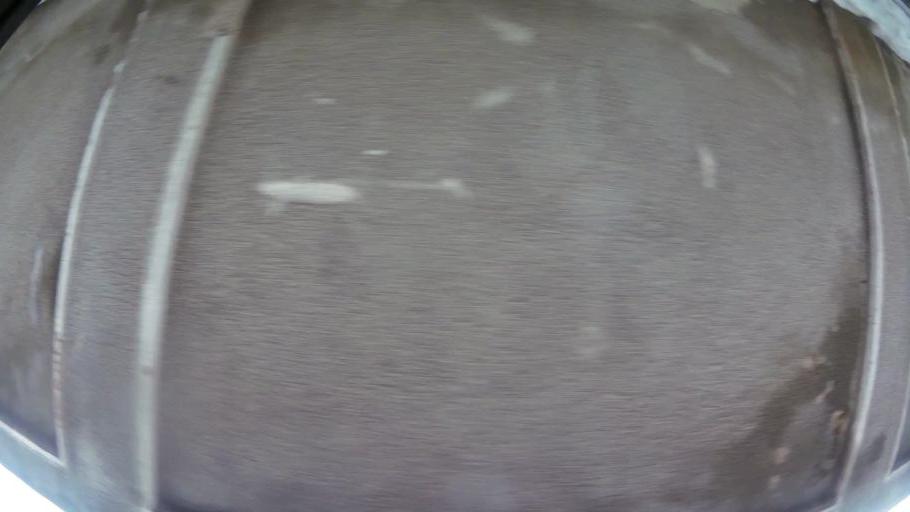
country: RO
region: Bucuresti
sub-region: Municipiul Bucuresti
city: Bucuresti
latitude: 44.4203
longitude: 26.0554
